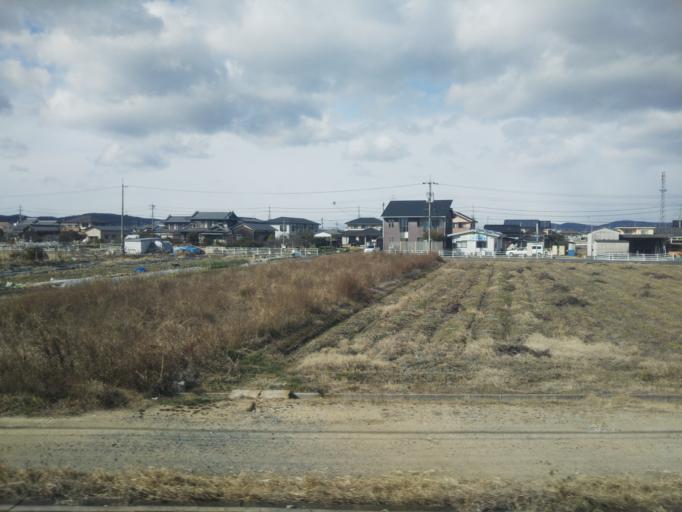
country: JP
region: Okayama
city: Okayama-shi
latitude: 34.6073
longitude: 133.8678
